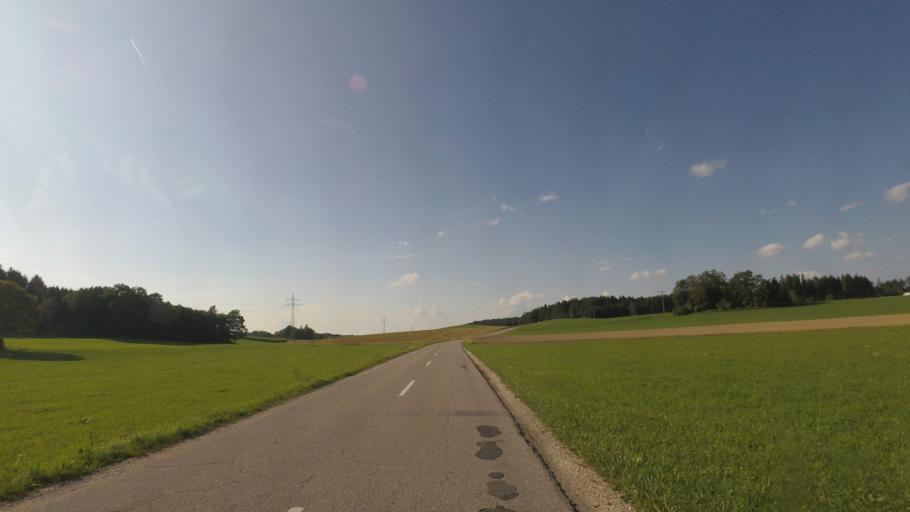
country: DE
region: Bavaria
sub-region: Upper Bavaria
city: Traunstein
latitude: 47.8832
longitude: 12.6180
